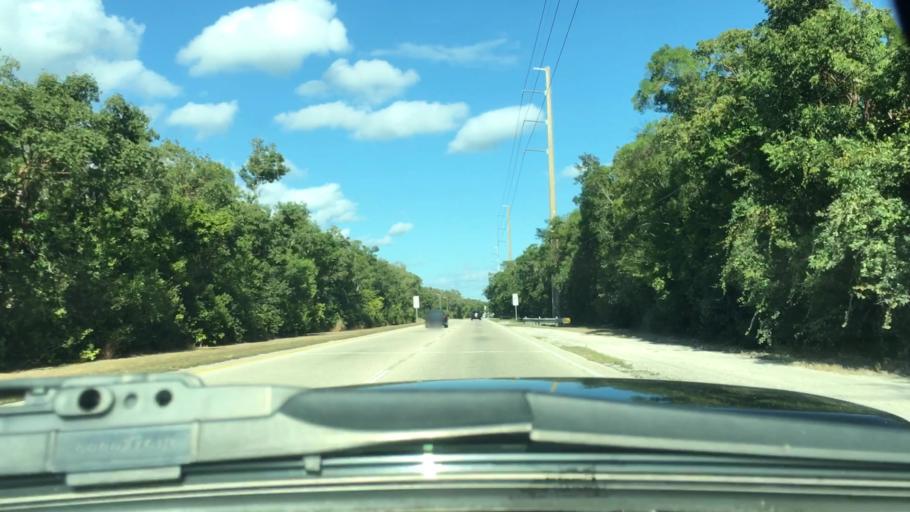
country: US
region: Florida
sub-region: Monroe County
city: Key Largo
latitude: 25.0695
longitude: -80.4671
